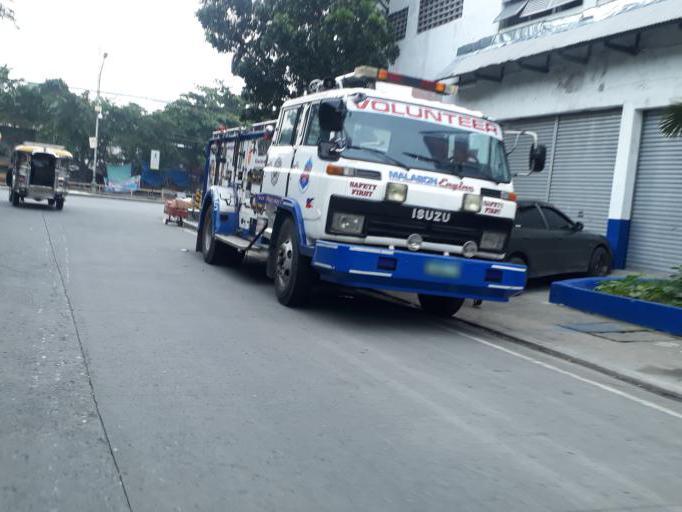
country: PH
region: Metro Manila
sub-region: Caloocan City
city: Niugan
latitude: 14.6590
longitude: 120.9618
